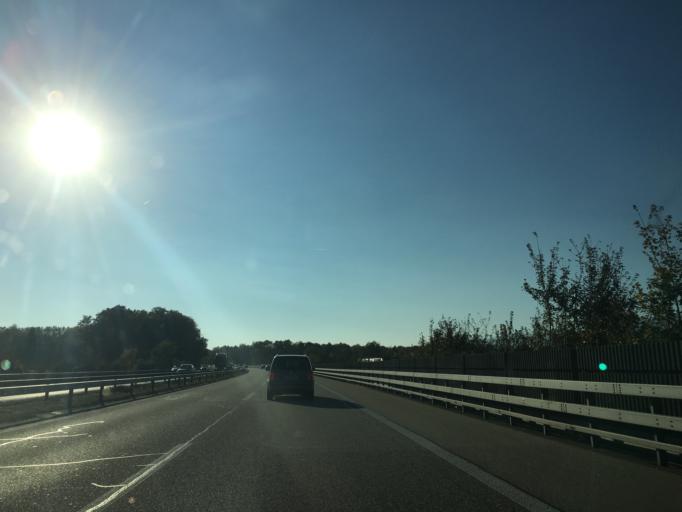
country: CH
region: Solothurn
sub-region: Bezirk Wasseramt
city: Luterbach
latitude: 47.2096
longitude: 7.5850
